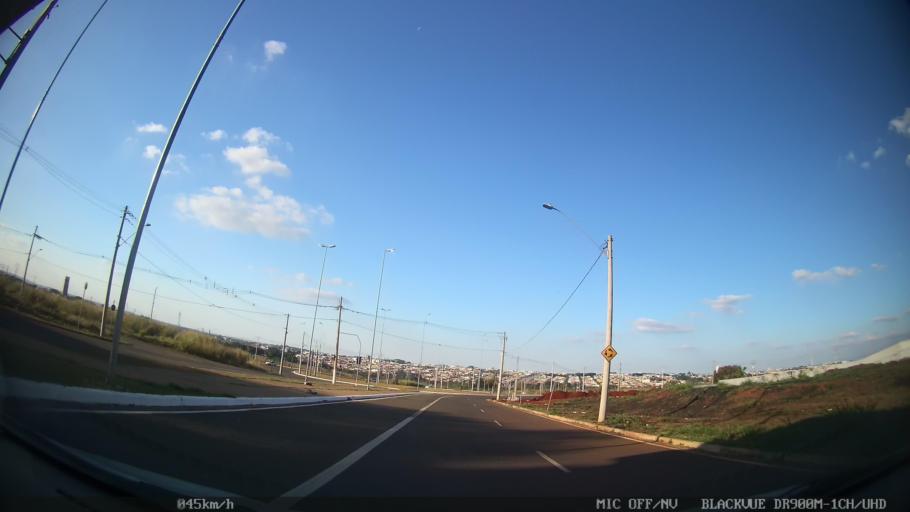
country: BR
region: Sao Paulo
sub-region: Santa Barbara D'Oeste
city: Santa Barbara d'Oeste
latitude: -22.7482
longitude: -47.3990
